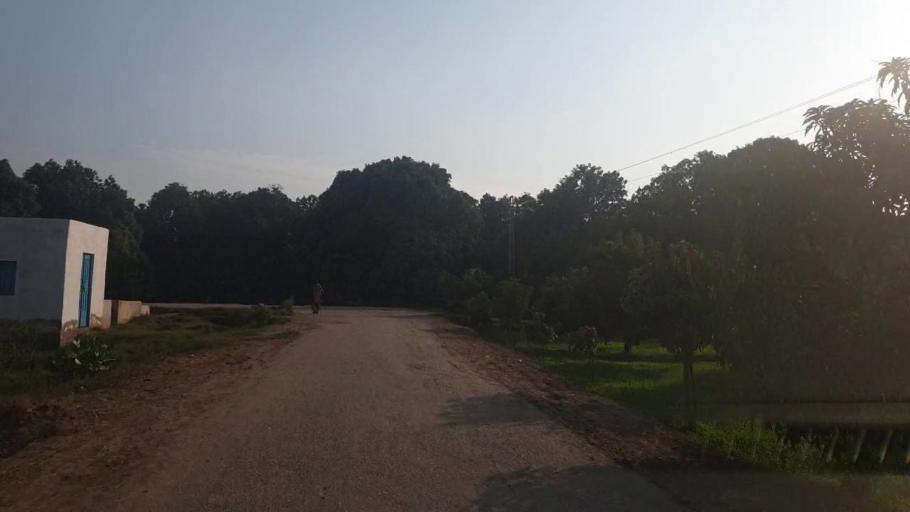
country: PK
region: Sindh
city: Tando Jam
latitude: 25.4241
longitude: 68.4640
